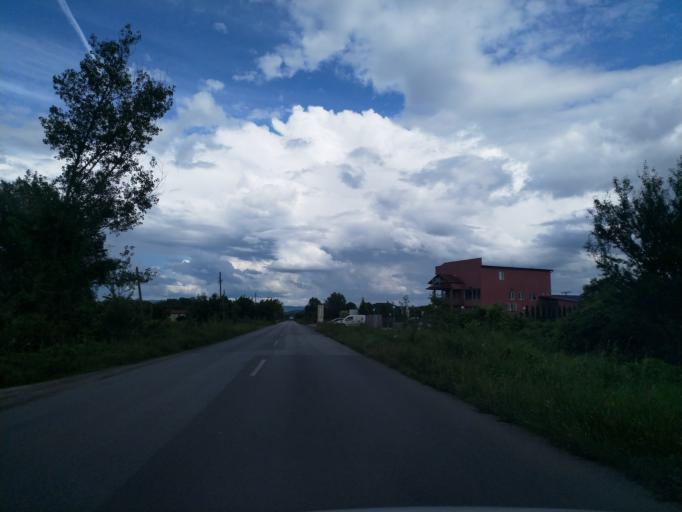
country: RS
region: Central Serbia
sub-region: Pomoravski Okrug
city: Cuprija
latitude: 43.9435
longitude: 21.3492
